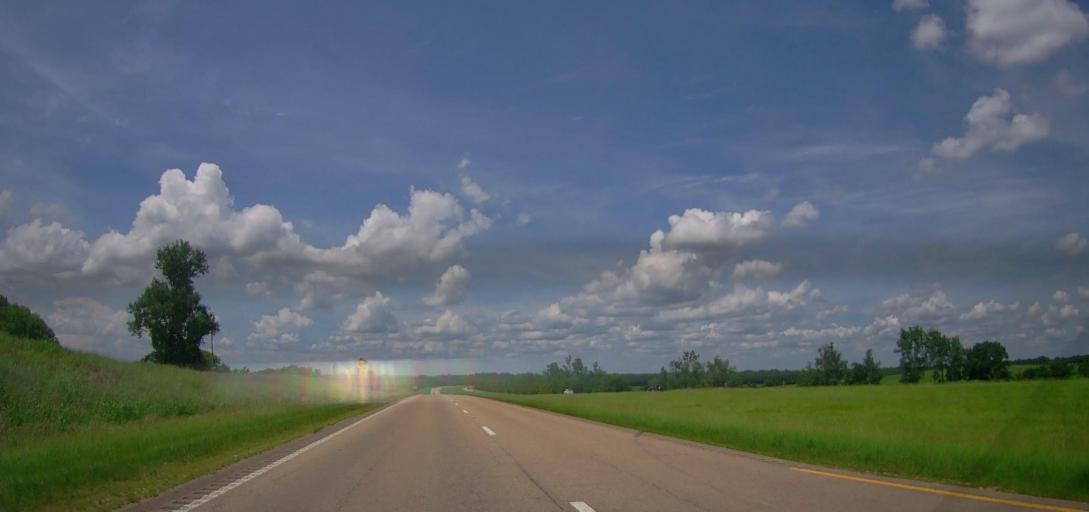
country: US
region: Mississippi
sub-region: Lee County
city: Nettleton
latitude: 34.0423
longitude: -88.6323
